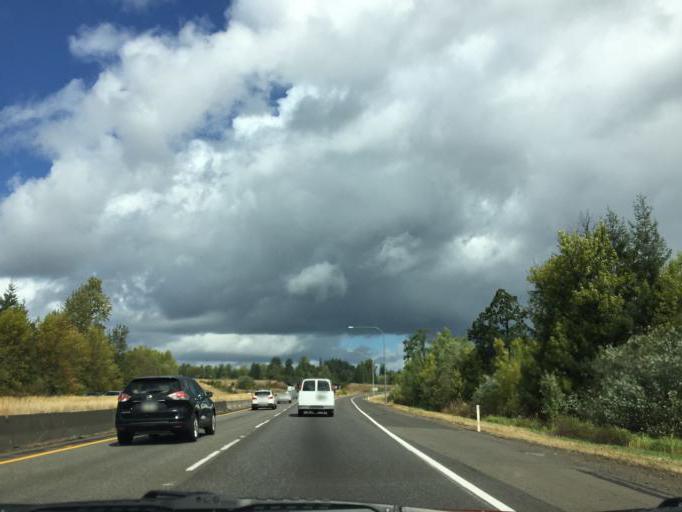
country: US
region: Washington
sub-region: Lewis County
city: Winlock
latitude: 46.4706
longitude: -122.8840
